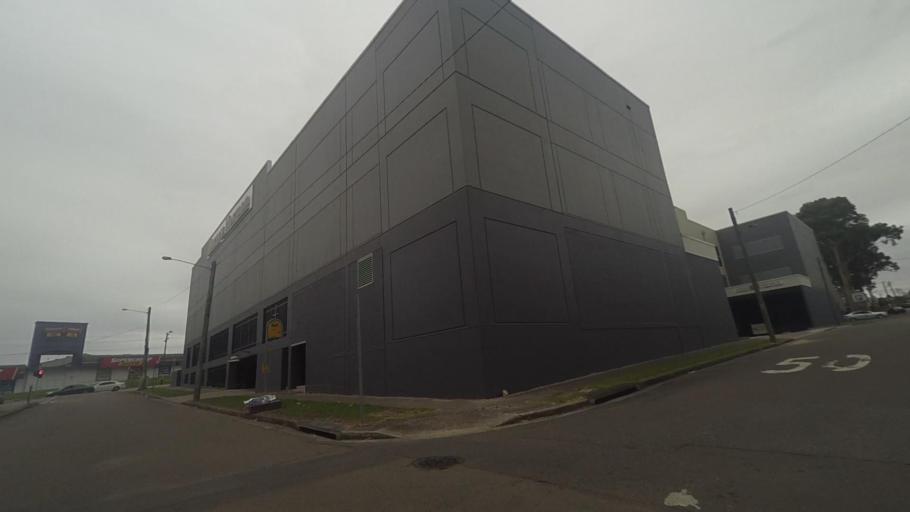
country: AU
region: New South Wales
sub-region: Auburn
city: Auburn
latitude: -33.8402
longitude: 151.0313
